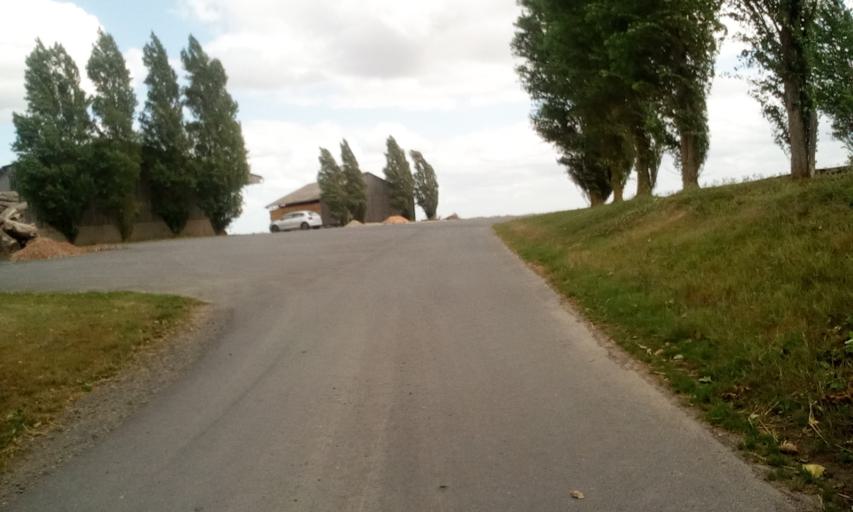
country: FR
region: Lower Normandy
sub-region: Departement du Calvados
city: Ver-sur-Mer
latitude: 49.3111
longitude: -0.5452
